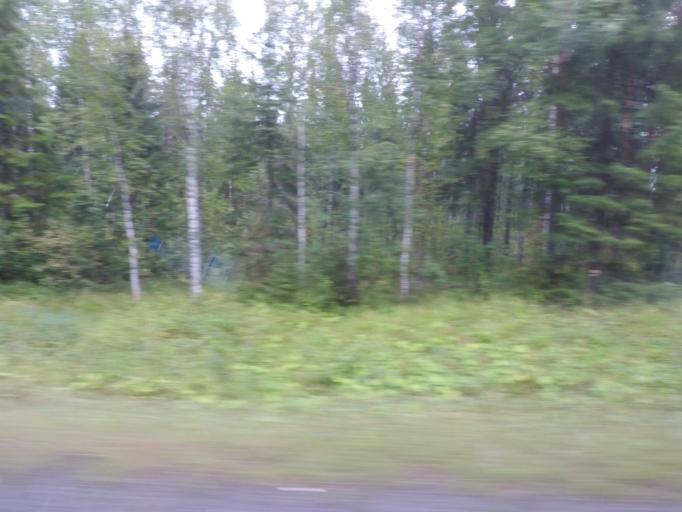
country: FI
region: Southern Savonia
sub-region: Pieksaemaeki
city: Joroinen
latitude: 62.1263
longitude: 27.8394
